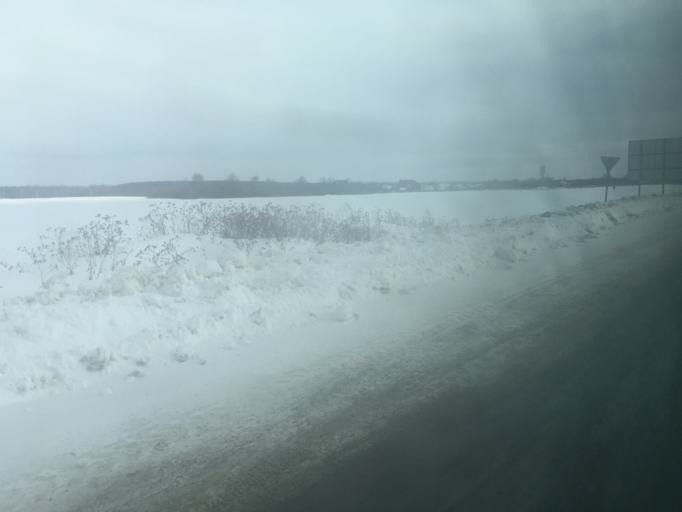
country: RU
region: Tatarstan
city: Nizhniye Vyazovyye
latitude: 55.7635
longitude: 48.5361
